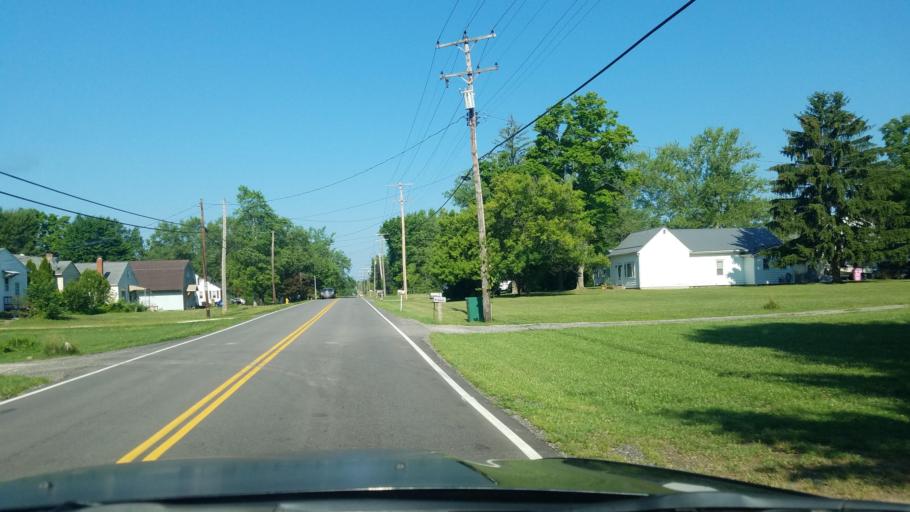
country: US
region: Ohio
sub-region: Trumbull County
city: Champion Heights
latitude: 41.2915
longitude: -80.8354
